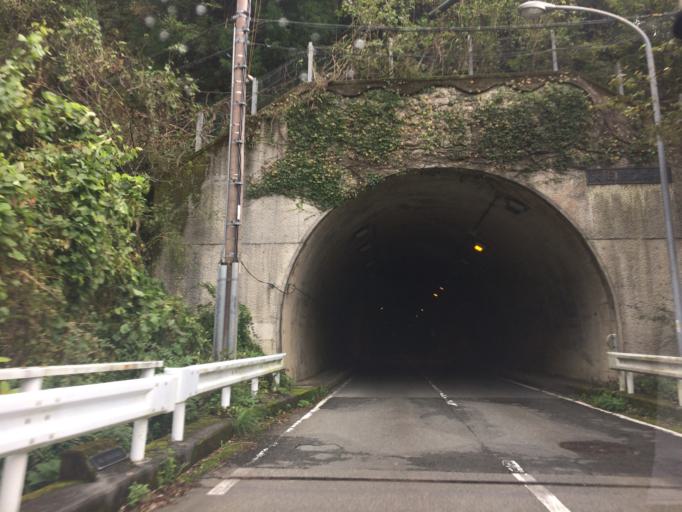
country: JP
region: Shizuoka
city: Shizuoka-shi
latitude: 35.1687
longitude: 138.1571
